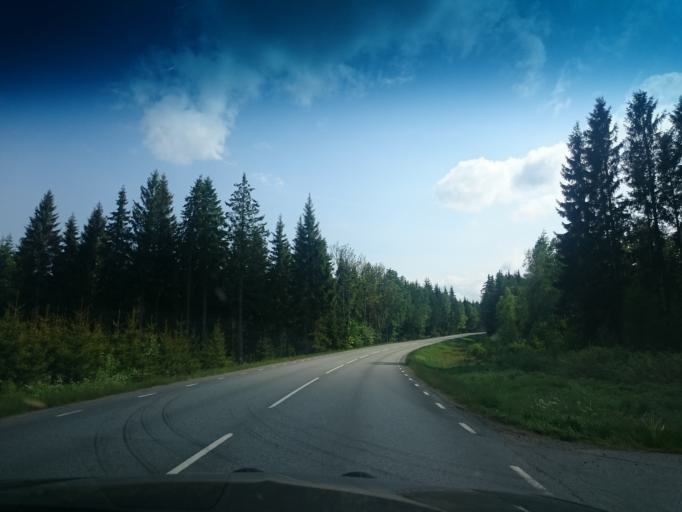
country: SE
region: Joenkoeping
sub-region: Vetlanda Kommun
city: Vetlanda
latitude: 57.4100
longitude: 15.0022
